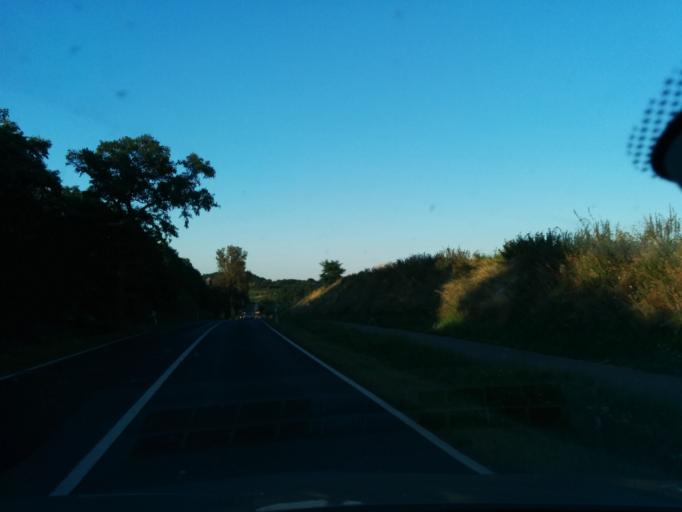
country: DE
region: Mecklenburg-Vorpommern
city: Loddin
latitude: 53.9550
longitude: 14.0572
